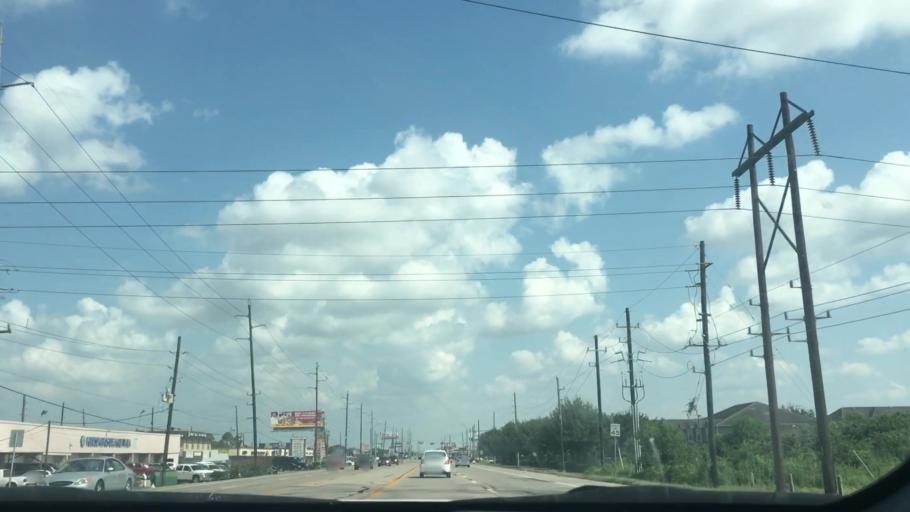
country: US
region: Texas
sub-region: Fort Bend County
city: Stafford
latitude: 29.6056
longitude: -95.5644
